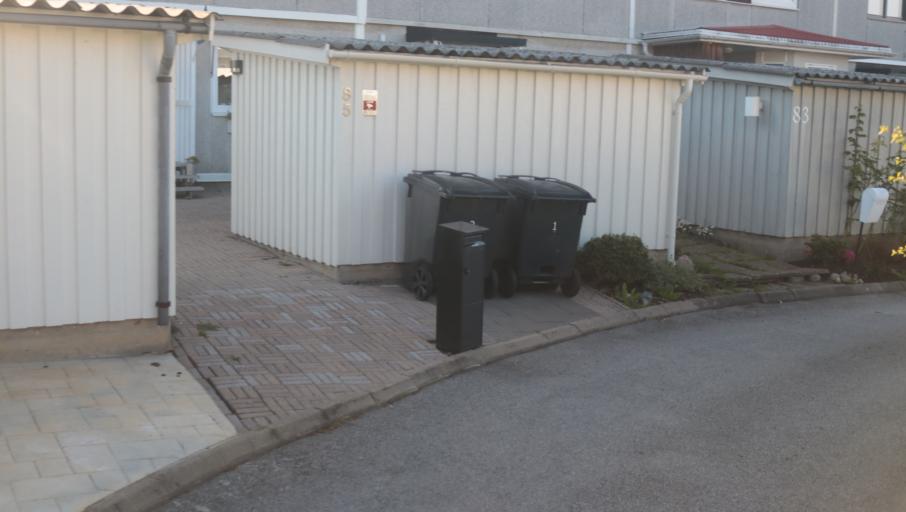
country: SE
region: Blekinge
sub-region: Karlshamns Kommun
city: Karlshamn
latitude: 56.1853
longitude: 14.8565
